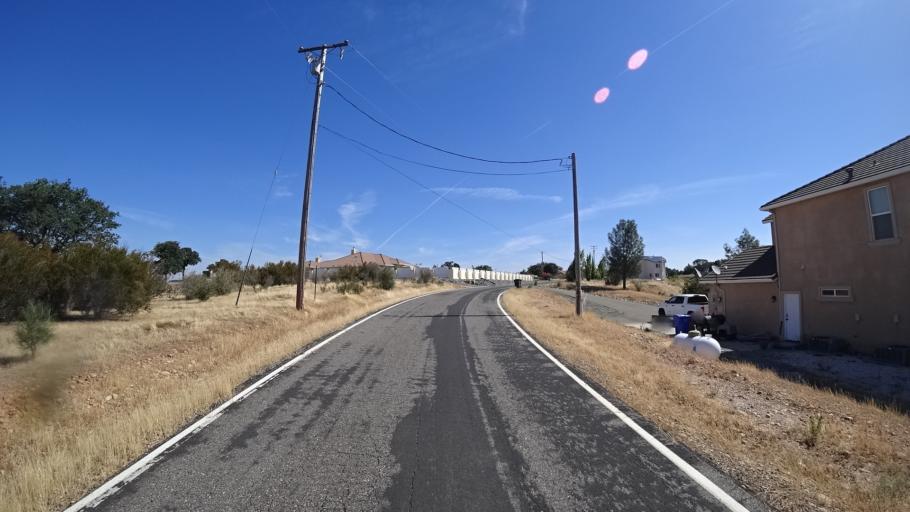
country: US
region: California
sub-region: Calaveras County
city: Valley Springs
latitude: 38.1701
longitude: -120.8665
